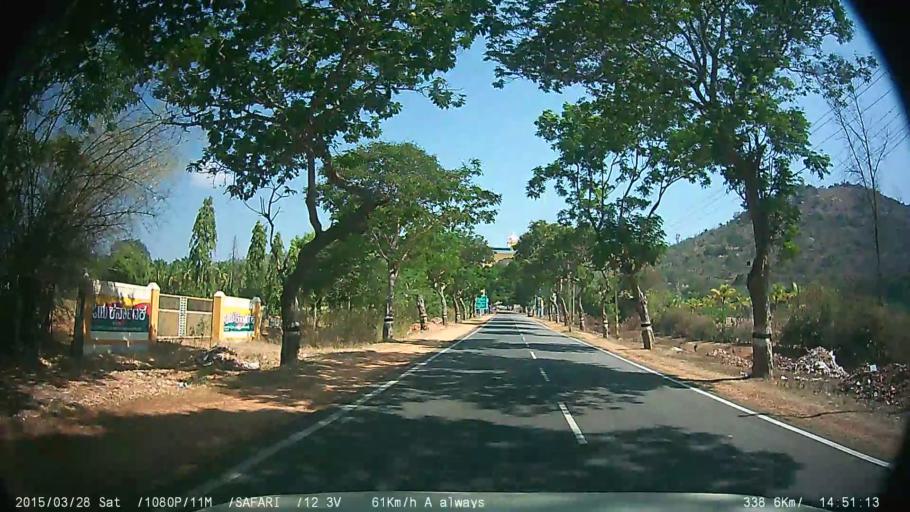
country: IN
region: Karnataka
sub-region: Mysore
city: Mysore
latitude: 12.2910
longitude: 76.6839
